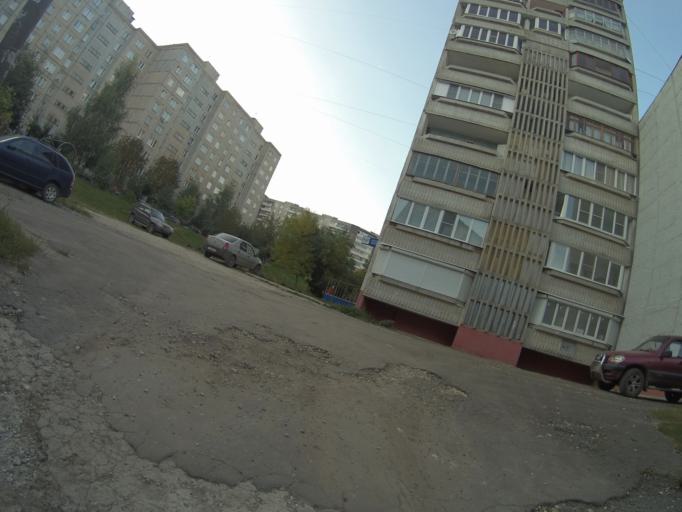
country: RU
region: Vladimir
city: Vladimir
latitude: 56.1052
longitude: 40.3530
